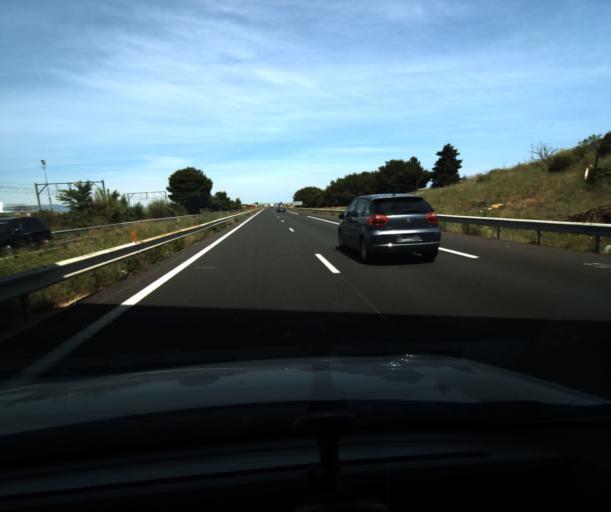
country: FR
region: Languedoc-Roussillon
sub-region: Departement des Pyrenees-Orientales
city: Perpignan
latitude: 42.7276
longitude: 2.8786
